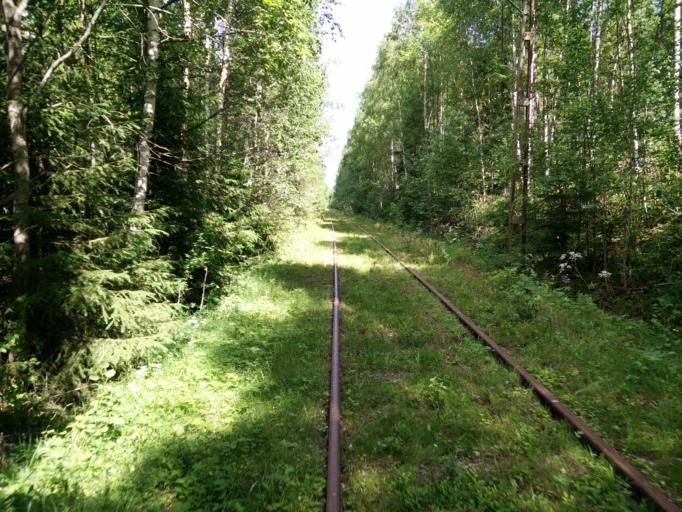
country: SE
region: Gaevleborg
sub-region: Hudiksvalls Kommun
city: Delsbo
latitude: 61.7979
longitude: 16.3866
